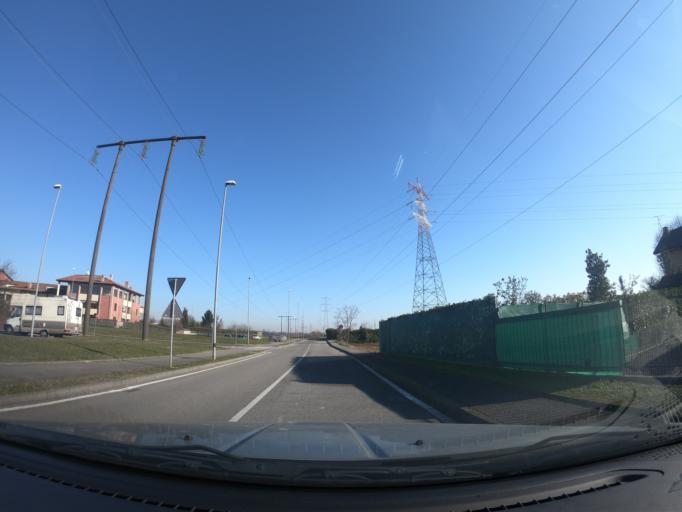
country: IT
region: Lombardy
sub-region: Provincia di Monza e Brianza
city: Sulbiate
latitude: 45.6373
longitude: 9.4297
